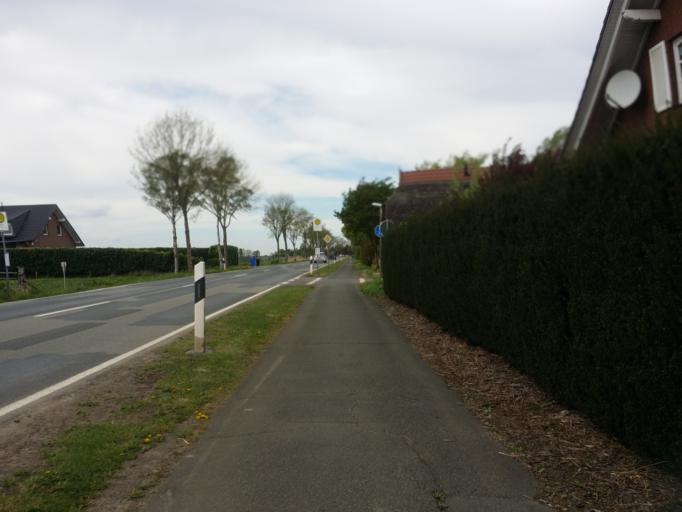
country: DE
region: Lower Saxony
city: Lemwerder
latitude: 53.1436
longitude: 8.5621
